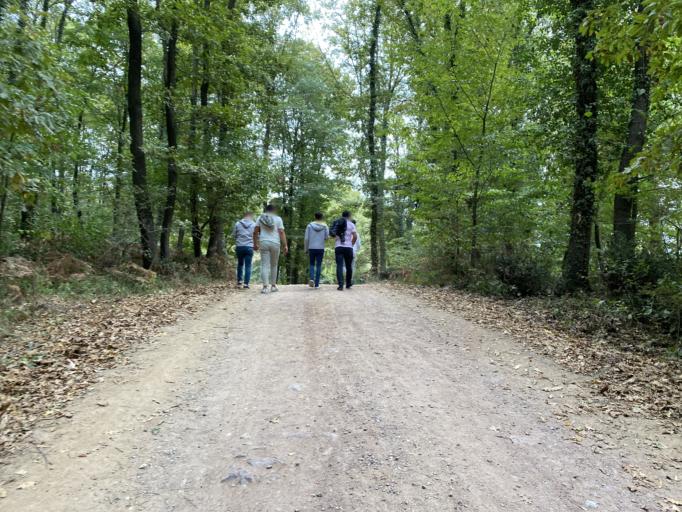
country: TR
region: Kocaeli
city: Derbent
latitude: 40.7350
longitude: 30.1604
